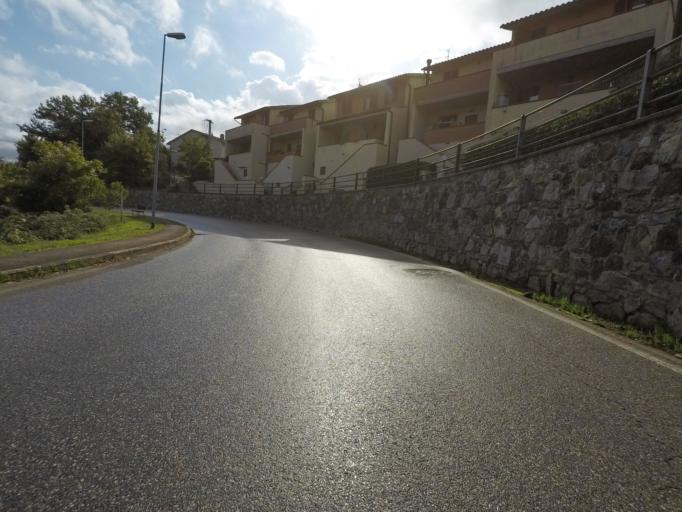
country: IT
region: Tuscany
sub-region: Provincia di Siena
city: Radda in Chianti
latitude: 43.4172
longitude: 11.3473
